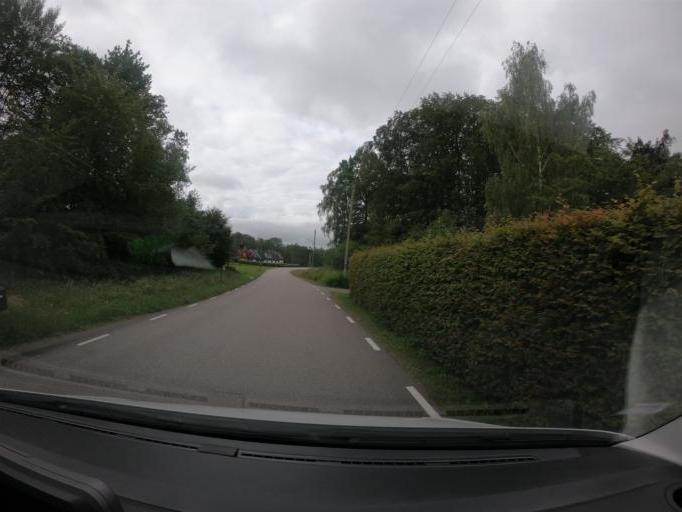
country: SE
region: Skane
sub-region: Angelholms Kommun
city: Munka-Ljungby
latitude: 56.3274
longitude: 12.9328
